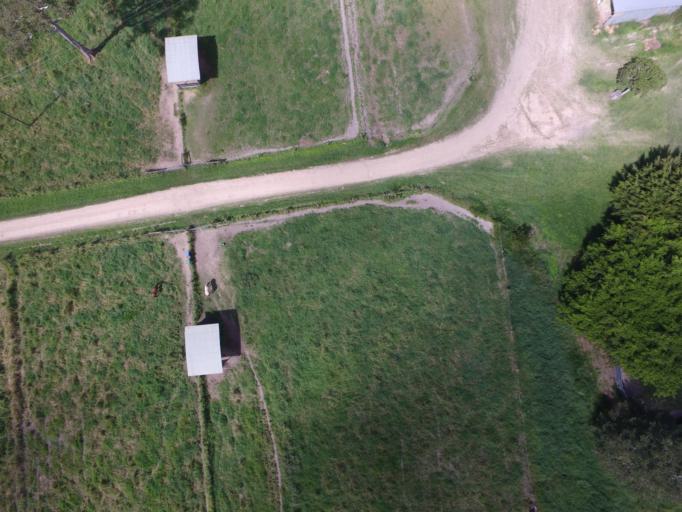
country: AU
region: Queensland
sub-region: Tablelands
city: Atherton
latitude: -17.3026
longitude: 145.4569
